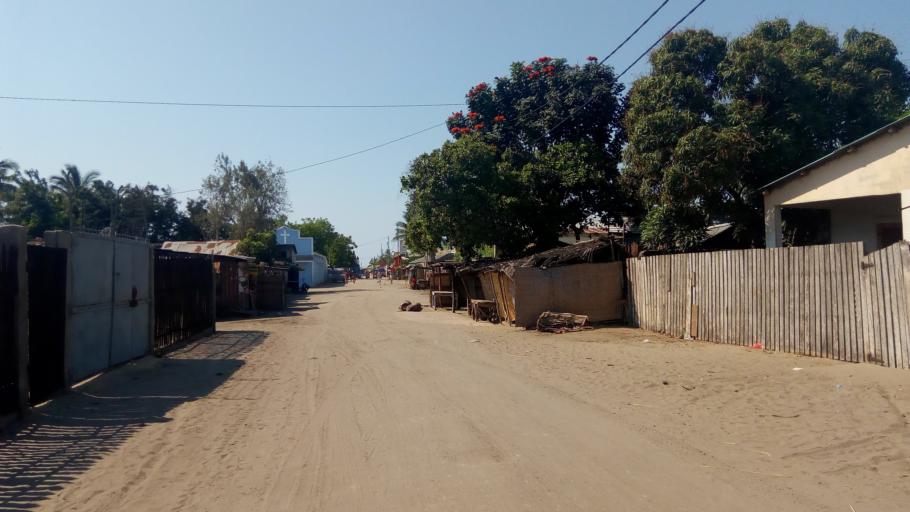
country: MG
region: Menabe
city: Morondava
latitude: -20.2957
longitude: 44.2786
